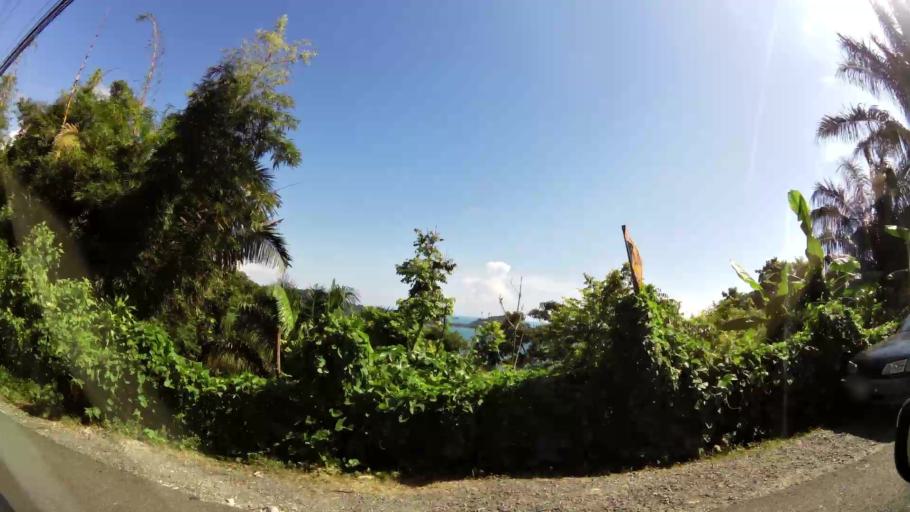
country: CR
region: Puntarenas
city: Quepos
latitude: 9.4009
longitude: -84.1633
